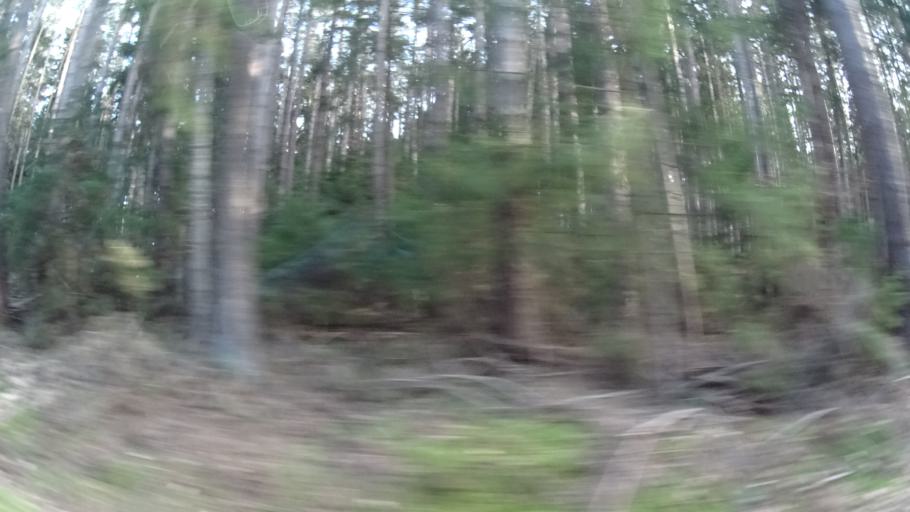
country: DE
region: Thuringia
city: Tonndorf
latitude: 50.8803
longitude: 11.2386
